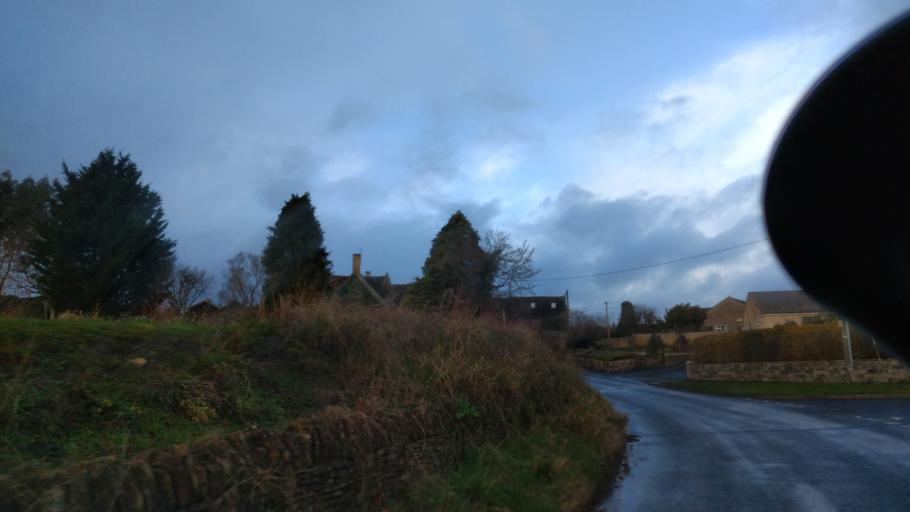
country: GB
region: England
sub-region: Wiltshire
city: Atworth
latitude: 51.3943
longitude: -2.1679
